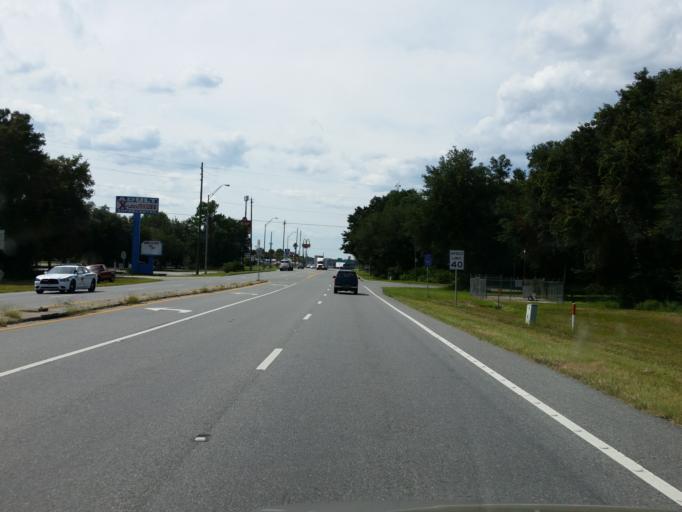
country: US
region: Florida
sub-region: Sumter County
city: Wildwood
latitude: 28.8717
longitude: -82.0860
